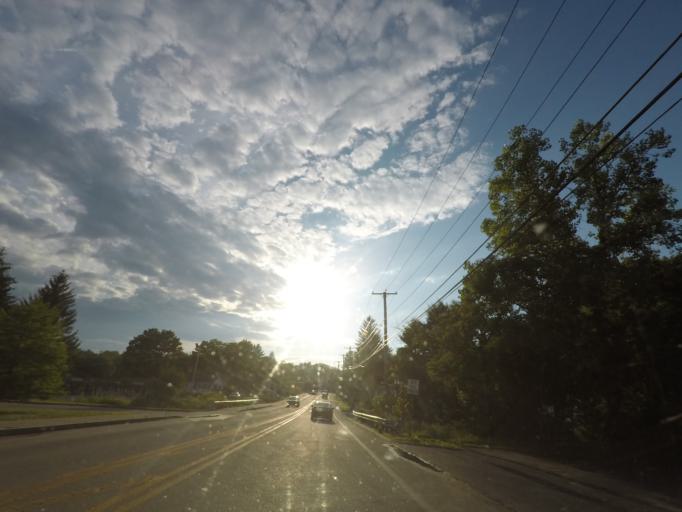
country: US
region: Massachusetts
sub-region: Worcester County
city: Sturbridge
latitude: 42.0878
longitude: -72.0624
